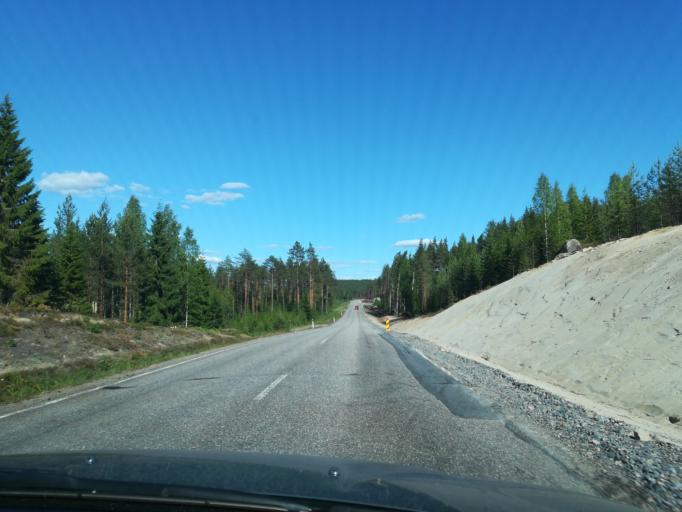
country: FI
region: Southern Savonia
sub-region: Mikkeli
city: Puumala
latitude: 61.4650
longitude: 28.3739
